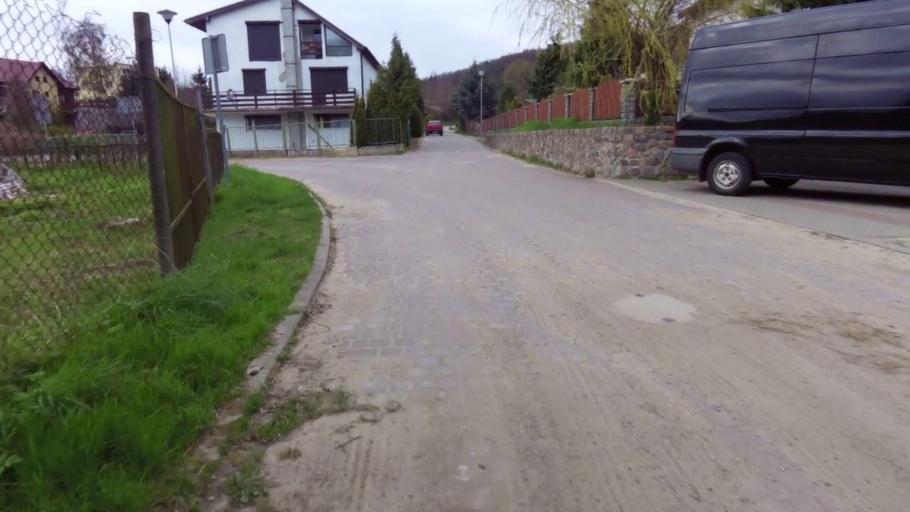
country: PL
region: West Pomeranian Voivodeship
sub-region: Powiat kamienski
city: Wolin
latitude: 53.9640
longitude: 14.5759
